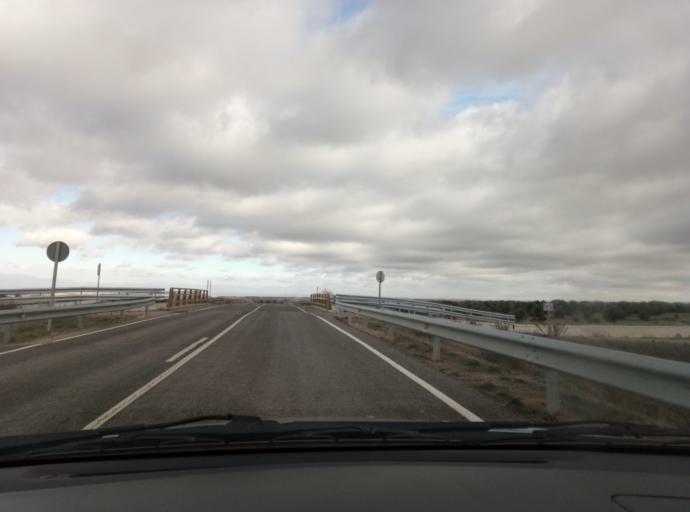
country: ES
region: Catalonia
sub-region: Provincia de Lleida
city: Vallbona de les Monges
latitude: 41.5664
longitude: 1.0687
